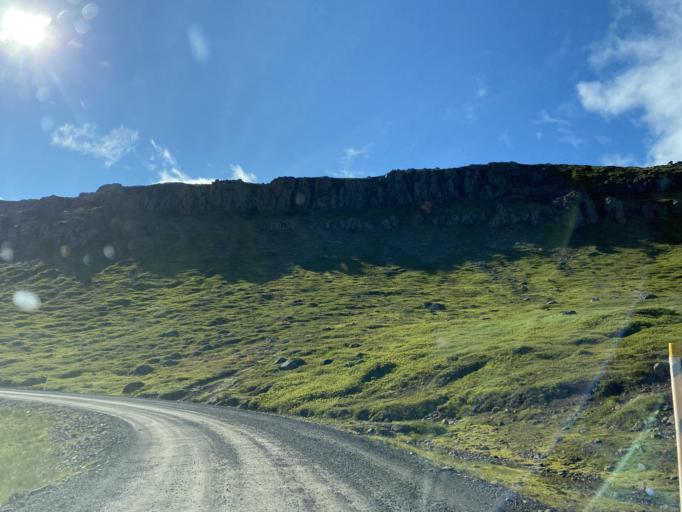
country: IS
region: East
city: Eskifjoerdur
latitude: 65.1802
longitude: -14.0938
